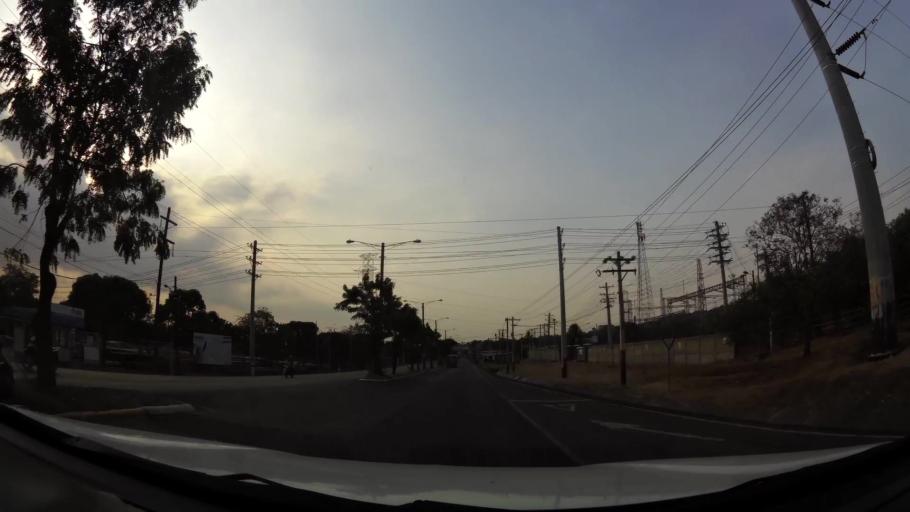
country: NI
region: Managua
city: Ciudad Sandino
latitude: 12.1661
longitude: -86.3414
